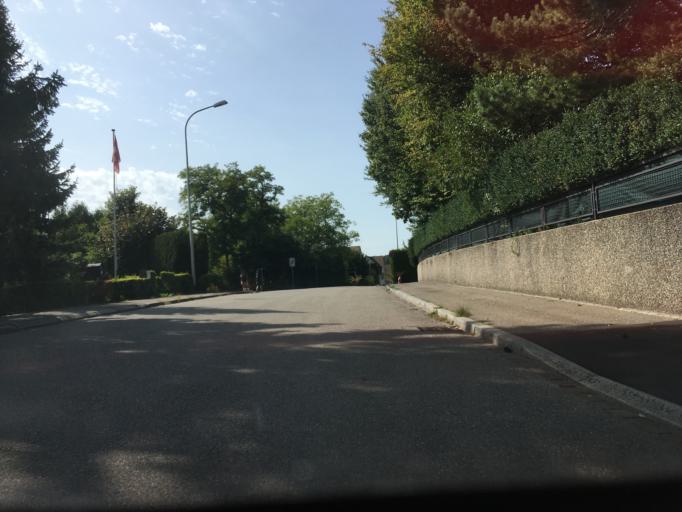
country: CH
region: Zurich
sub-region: Bezirk Buelach
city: Wallisellen / Rieden
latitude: 47.4208
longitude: 8.6033
